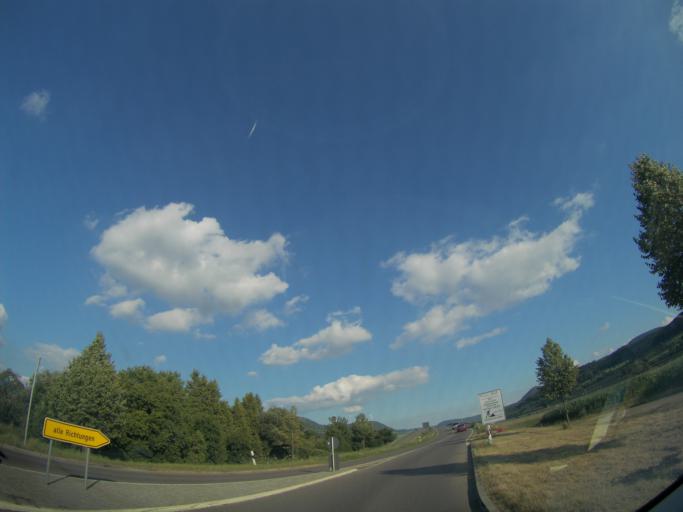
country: DE
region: Baden-Wuerttemberg
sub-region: Regierungsbezirk Stuttgart
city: Sussen
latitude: 48.6724
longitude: 9.7620
